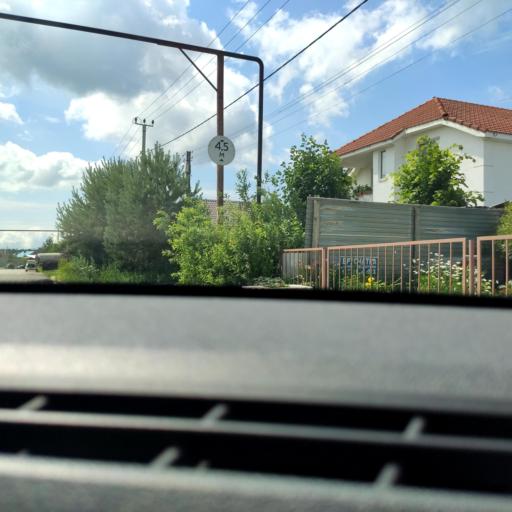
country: RU
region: Samara
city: Podstepki
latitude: 53.5705
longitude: 49.0807
